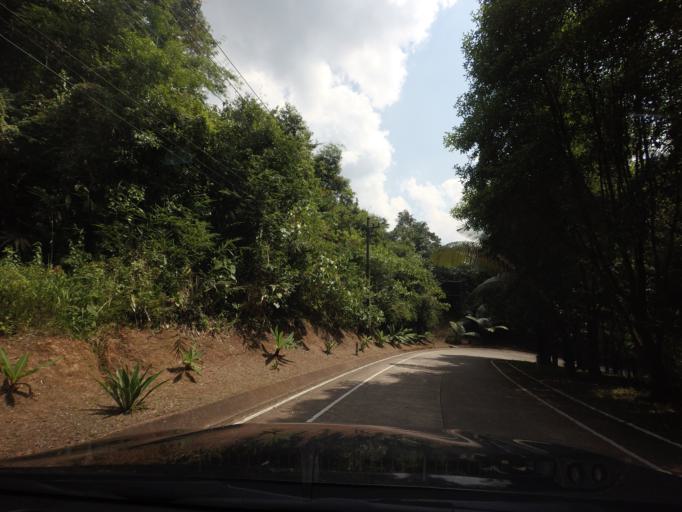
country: TH
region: Nan
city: Bo Kluea
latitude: 19.0196
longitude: 101.2091
